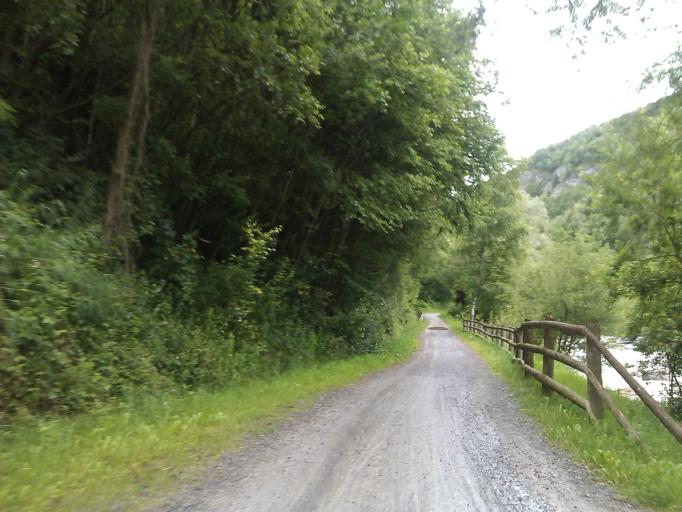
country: IT
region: Trentino-Alto Adige
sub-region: Bolzano
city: Silandro
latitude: 46.6140
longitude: 10.7374
